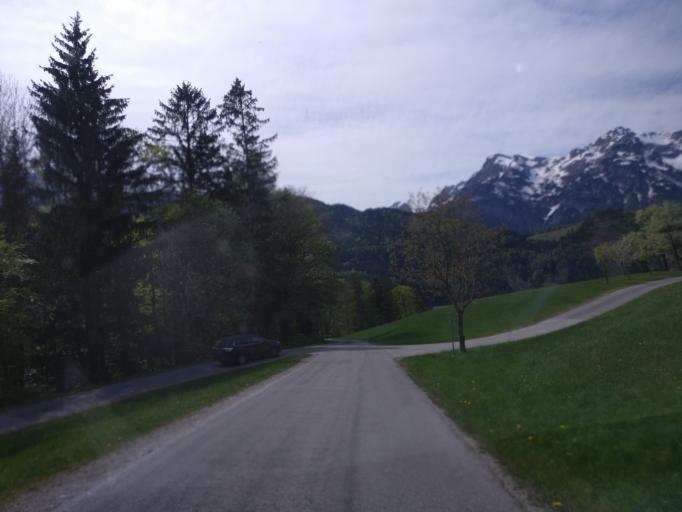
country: AT
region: Salzburg
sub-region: Politischer Bezirk Sankt Johann im Pongau
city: Pfarrwerfen
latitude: 47.4727
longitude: 13.2031
